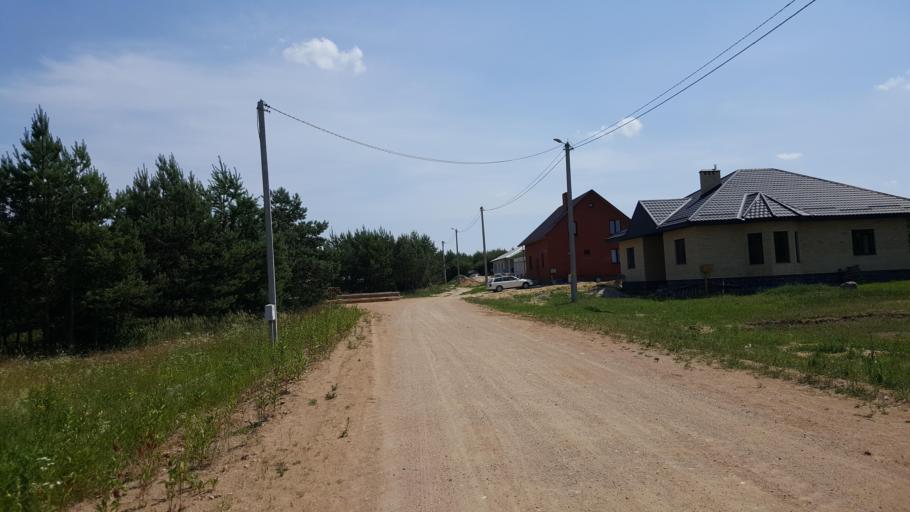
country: BY
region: Brest
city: Kamyanyets
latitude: 52.4062
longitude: 23.8437
